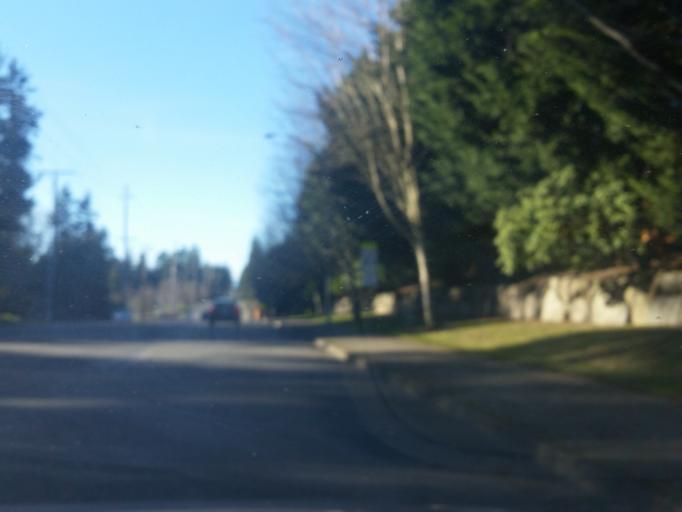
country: US
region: Washington
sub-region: Snohomish County
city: Meadowdale
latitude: 47.8467
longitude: -122.3099
